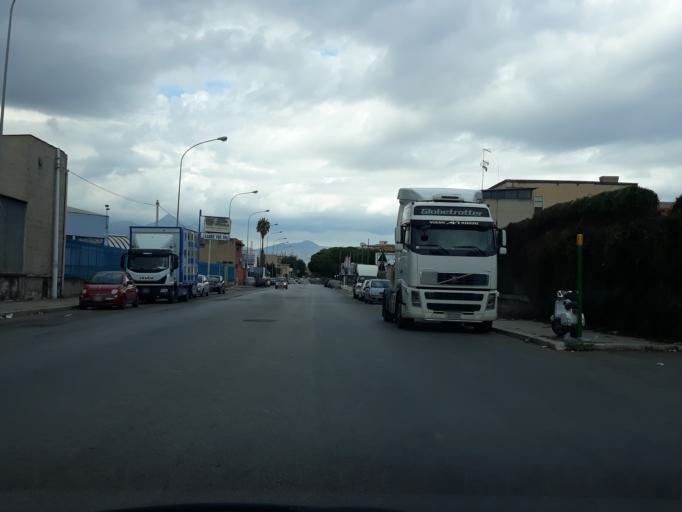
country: IT
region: Sicily
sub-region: Palermo
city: Ciaculli
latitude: 38.0944
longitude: 13.4015
